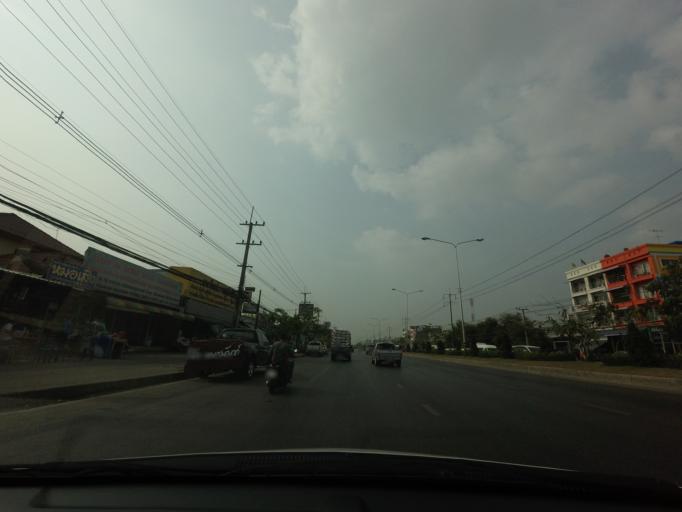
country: TH
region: Bangkok
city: Nong Khaem
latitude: 13.7403
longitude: 100.3292
